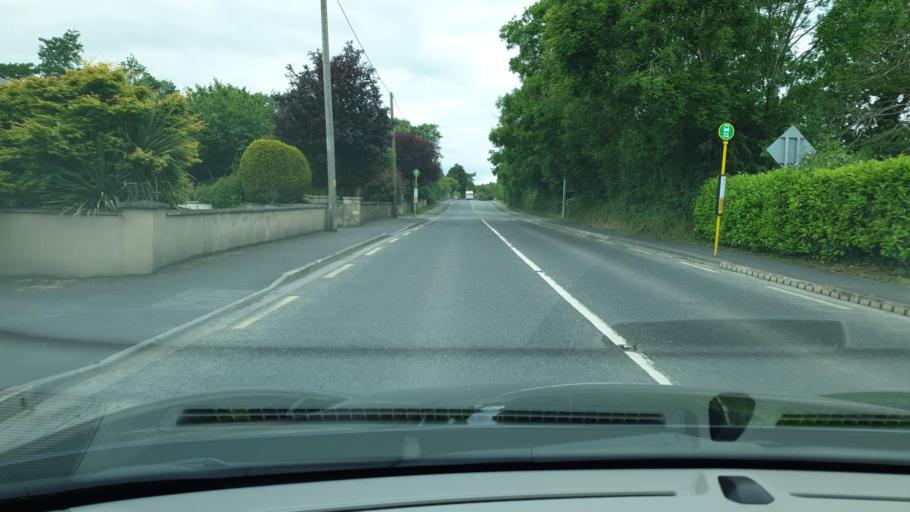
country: IE
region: Leinster
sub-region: An Mhi
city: Dunboyne
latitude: 53.4149
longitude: -6.4516
